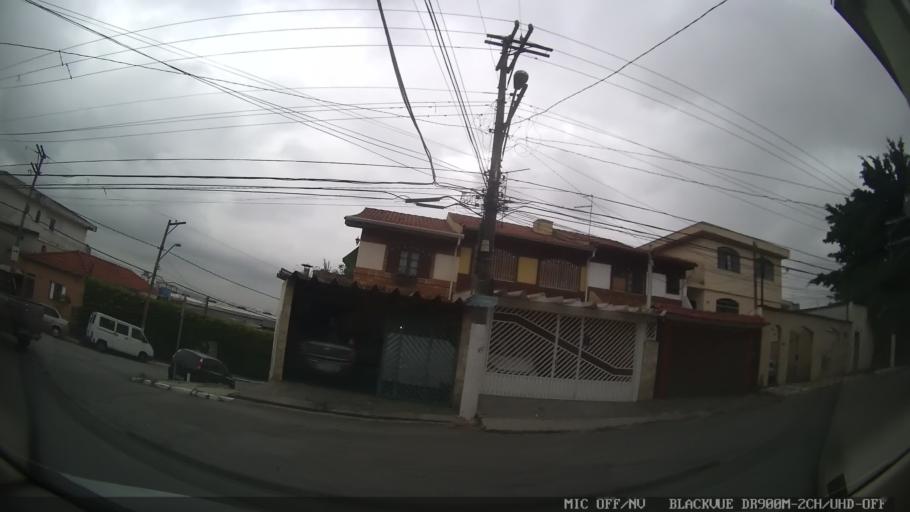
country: BR
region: Sao Paulo
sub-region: Sao Paulo
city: Sao Paulo
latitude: -23.4943
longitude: -46.6032
